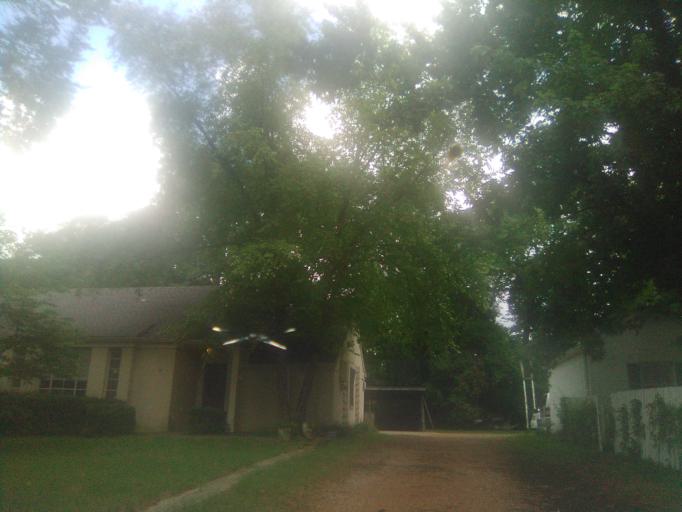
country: US
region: Tennessee
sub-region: Davidson County
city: Belle Meade
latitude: 36.1100
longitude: -86.8404
